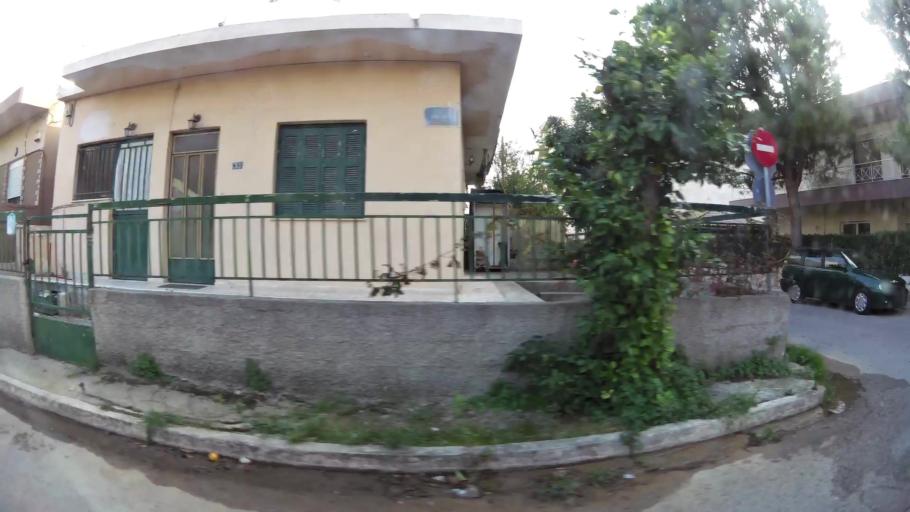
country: GR
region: Attica
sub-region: Nomarchia Anatolikis Attikis
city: Acharnes
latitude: 38.0853
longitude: 23.7421
